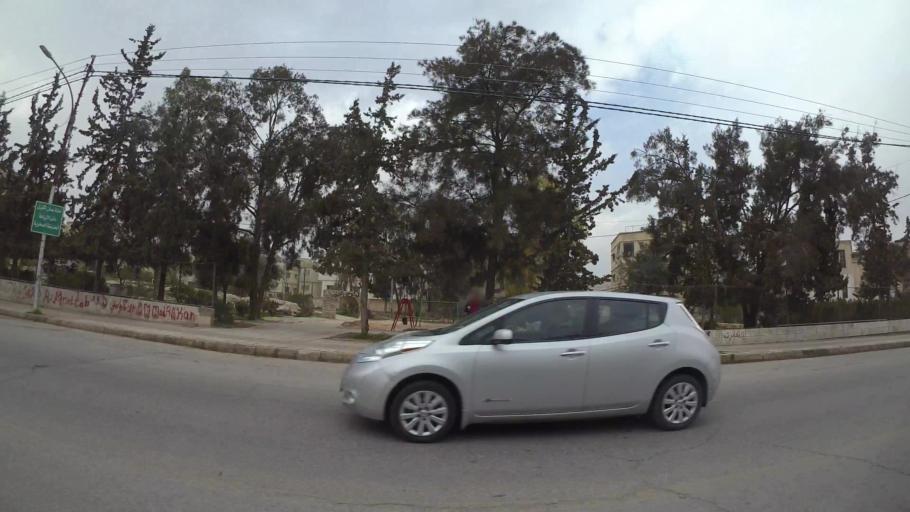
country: JO
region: Amman
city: Amman
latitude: 31.9630
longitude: 35.9376
